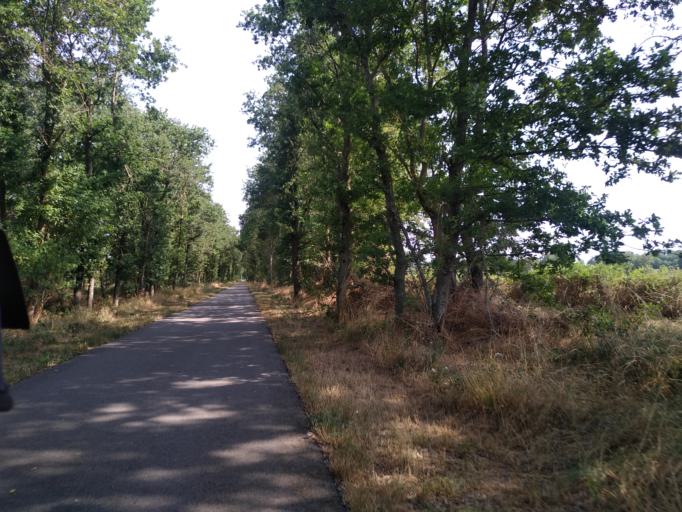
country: FR
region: Bourgogne
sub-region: Departement de Saone-et-Loire
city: Marcigny
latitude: 46.3356
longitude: 4.0284
